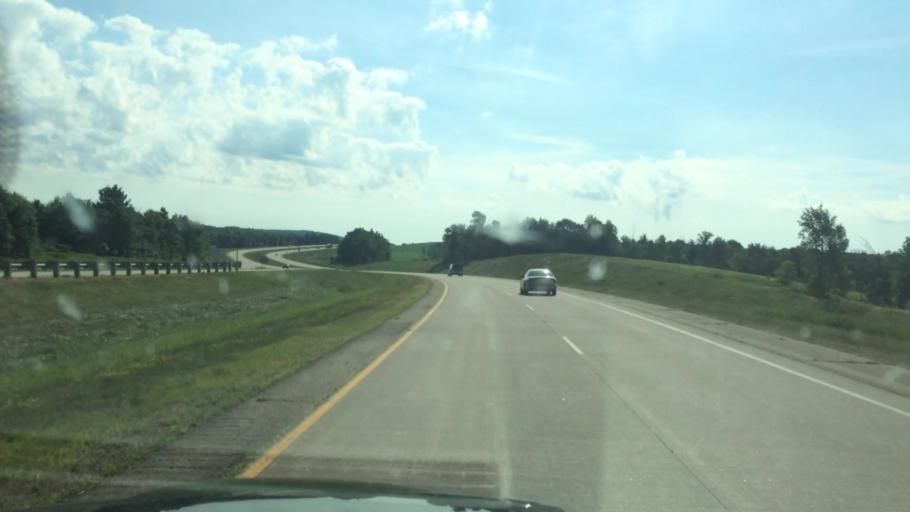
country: US
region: Wisconsin
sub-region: Shawano County
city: Wittenberg
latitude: 44.8237
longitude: -89.1220
